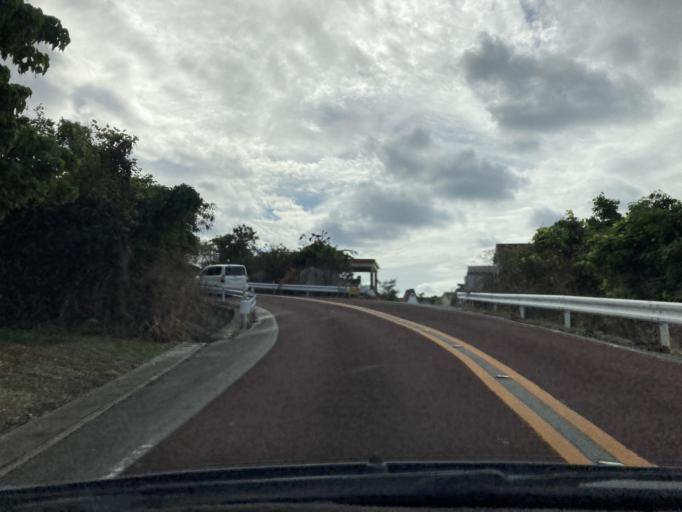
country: JP
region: Okinawa
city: Itoman
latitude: 26.1235
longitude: 127.6772
